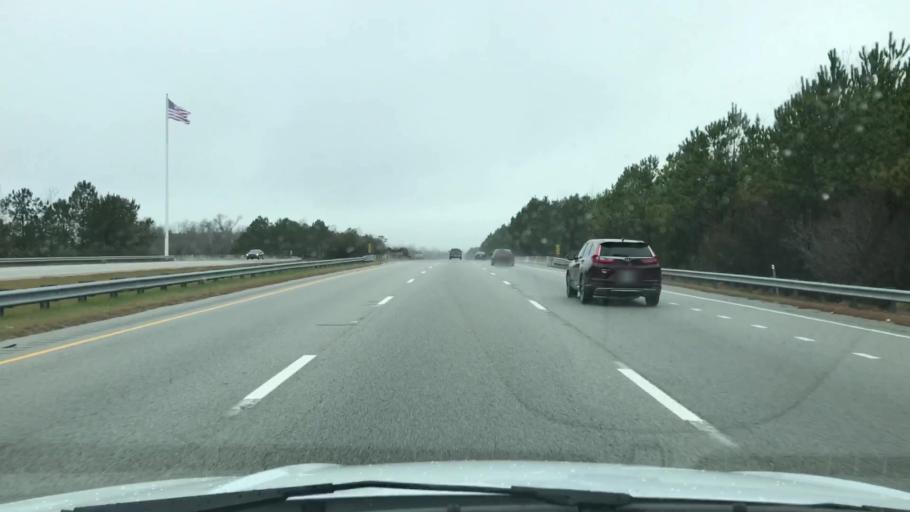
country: US
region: South Carolina
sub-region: Horry County
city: Myrtle Beach
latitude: 33.7511
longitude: -78.8673
